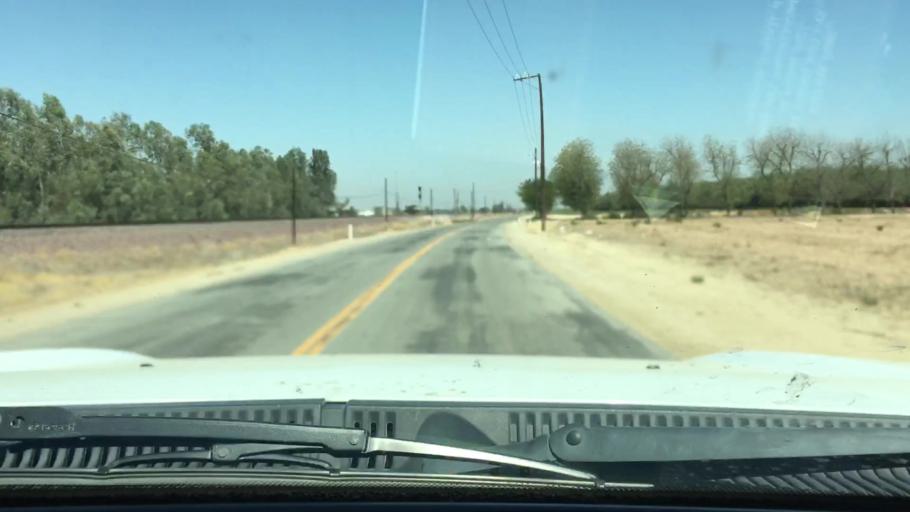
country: US
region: California
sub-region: Kern County
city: Wasco
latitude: 35.5624
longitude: -119.3317
